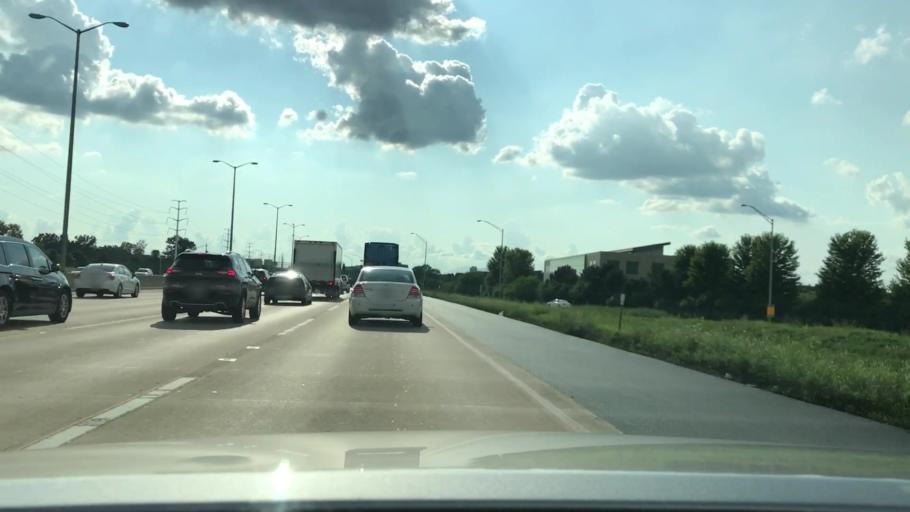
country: US
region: Illinois
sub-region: DuPage County
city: Warrenville
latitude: 41.8068
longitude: -88.1691
